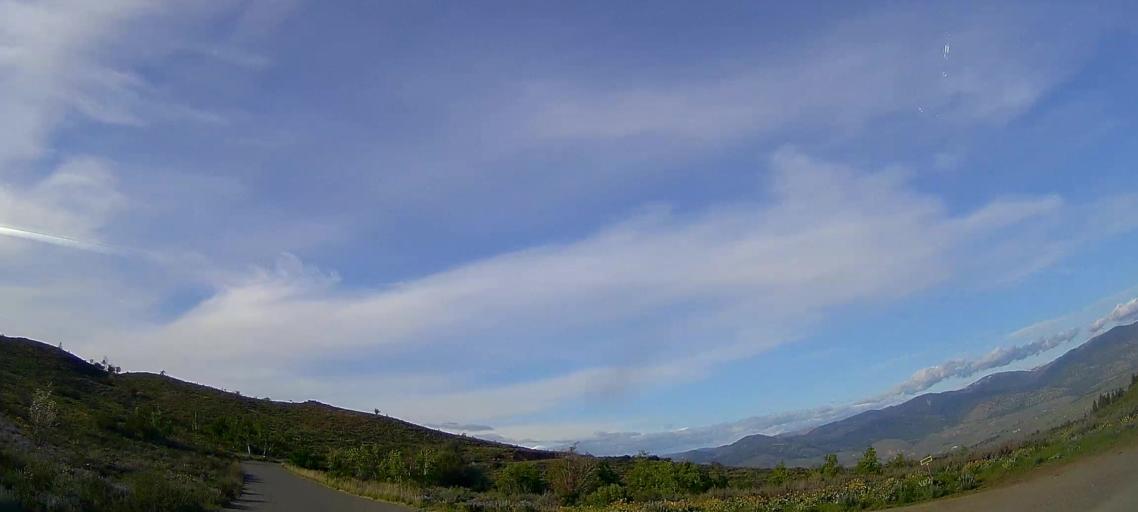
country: US
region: Washington
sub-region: Chelan County
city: Granite Falls
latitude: 48.4690
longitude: -120.2575
